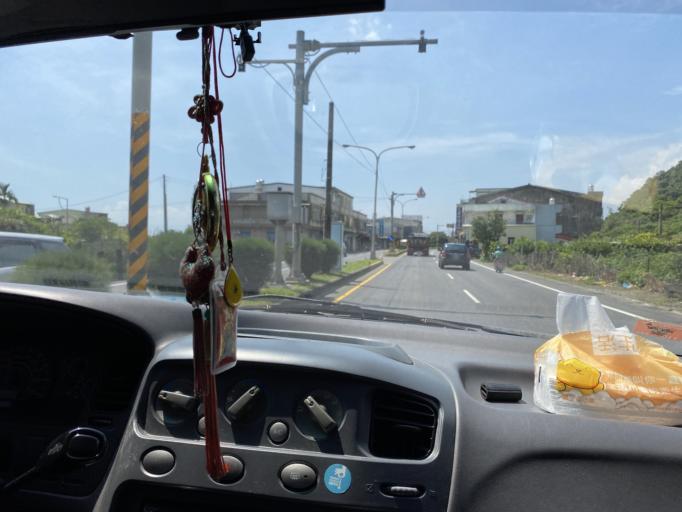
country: TW
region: Taiwan
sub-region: Yilan
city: Yilan
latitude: 24.8725
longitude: 121.8362
